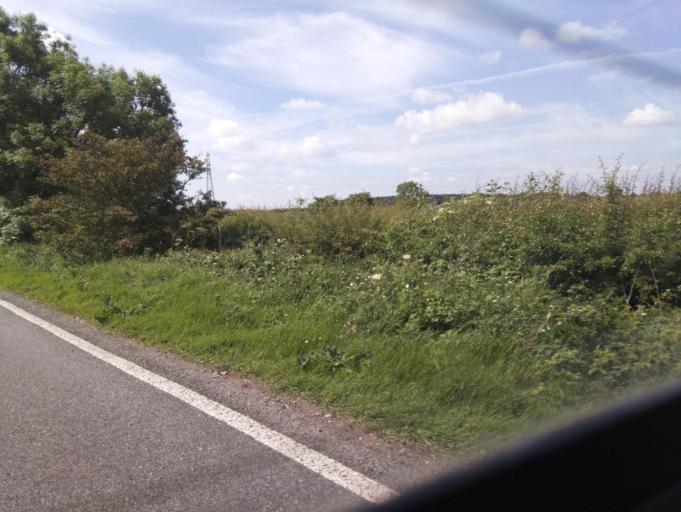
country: GB
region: England
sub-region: Lincolnshire
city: Burton
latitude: 53.2793
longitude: -0.5401
